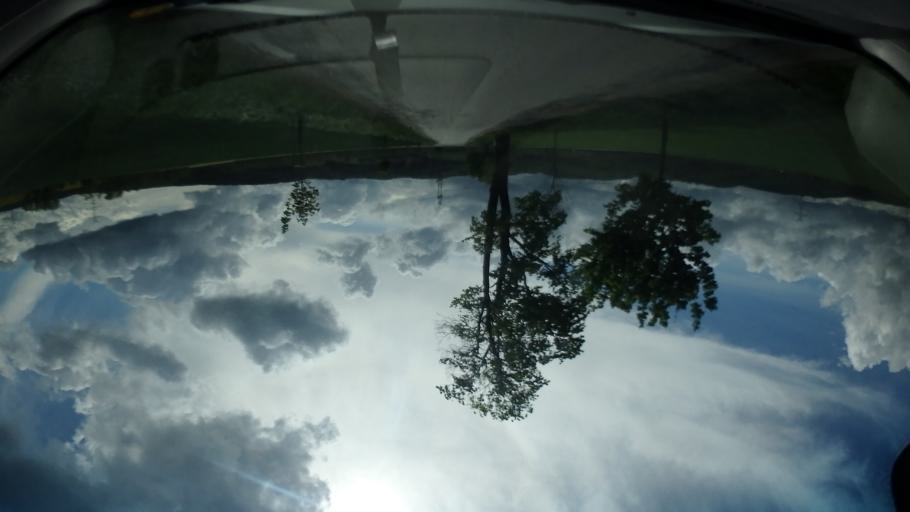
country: CZ
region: South Moravian
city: Ricany
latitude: 49.2279
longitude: 16.4169
